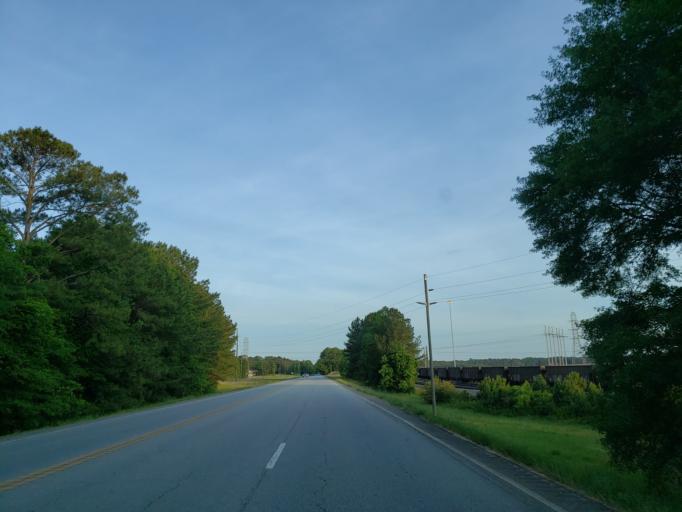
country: US
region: Georgia
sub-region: Coweta County
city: Newnan
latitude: 33.4620
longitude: -84.8914
